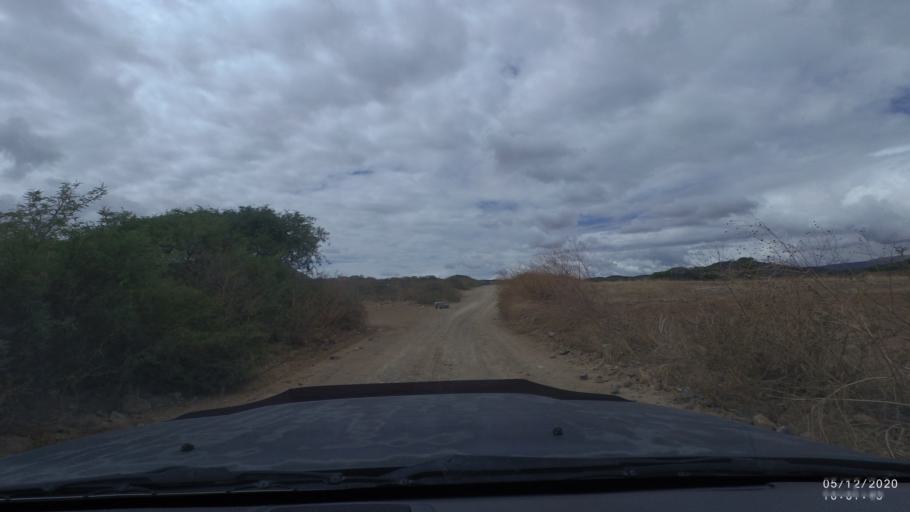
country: BO
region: Cochabamba
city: Sipe Sipe
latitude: -17.4440
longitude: -66.2871
